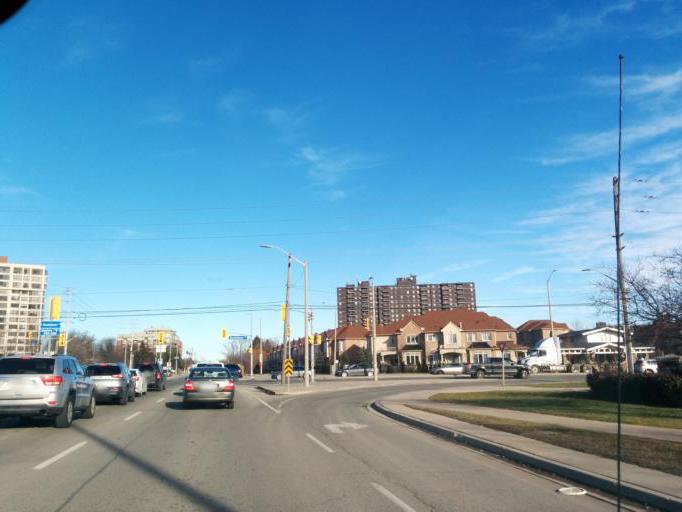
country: CA
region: Ontario
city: Mississauga
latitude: 43.5105
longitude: -79.6304
